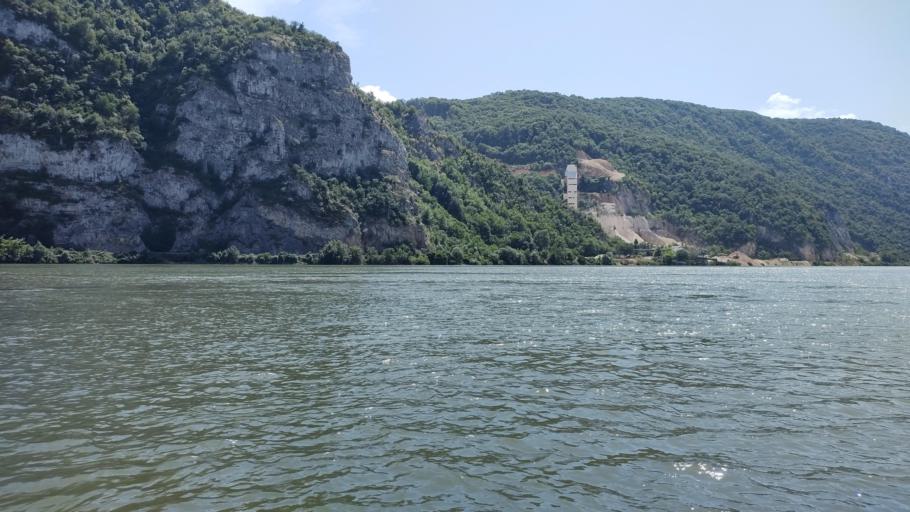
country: RO
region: Caras-Severin
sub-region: Comuna Pescari
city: Coronini
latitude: 44.6555
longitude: 21.7392
